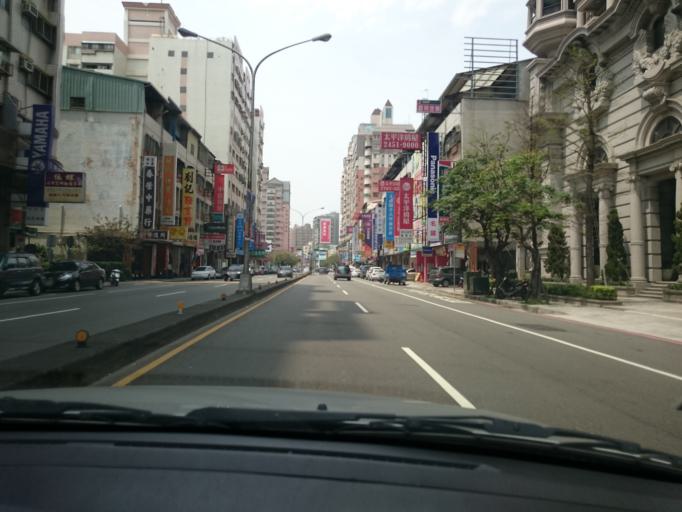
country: TW
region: Taiwan
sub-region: Taichung City
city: Taichung
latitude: 24.1693
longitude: 120.6467
